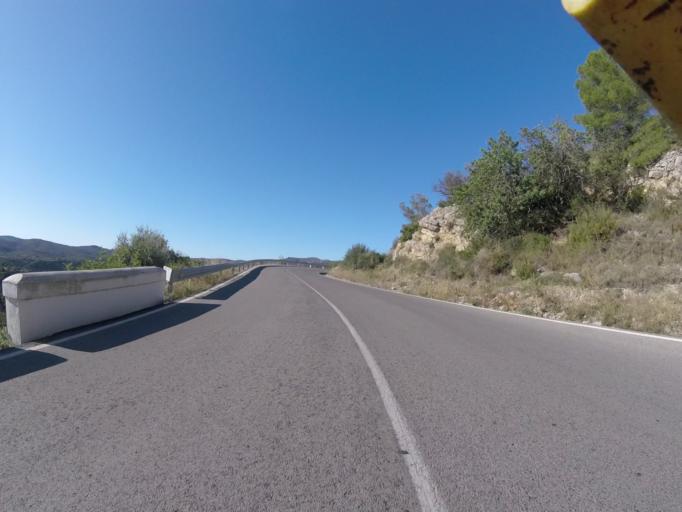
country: ES
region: Valencia
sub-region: Provincia de Castello
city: Cervera del Maestre
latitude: 40.4570
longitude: 0.2689
